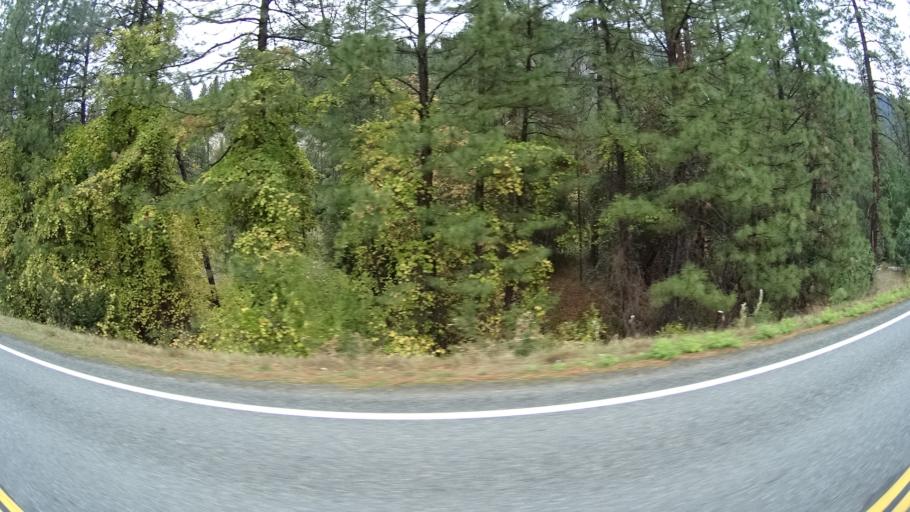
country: US
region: California
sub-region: Siskiyou County
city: Happy Camp
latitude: 41.8345
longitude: -123.1803
